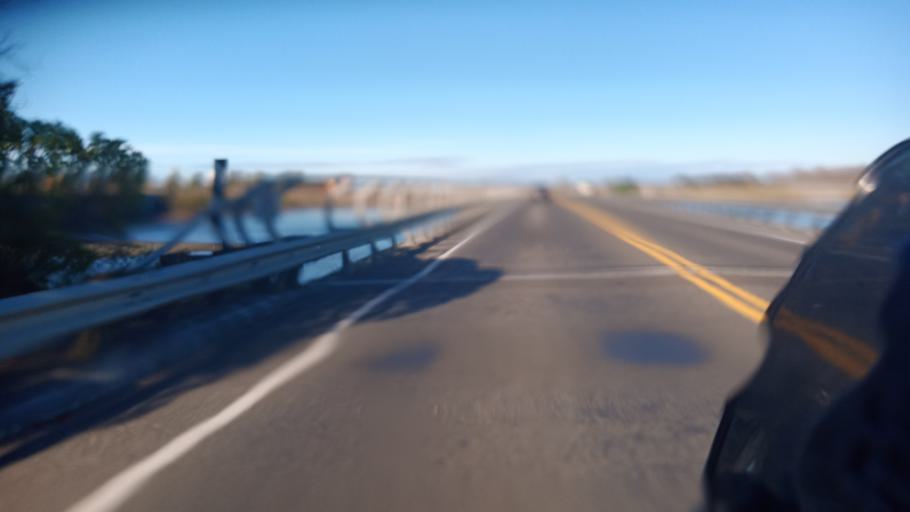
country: NZ
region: Hawke's Bay
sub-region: Napier City
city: Napier
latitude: -39.4847
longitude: 176.8765
